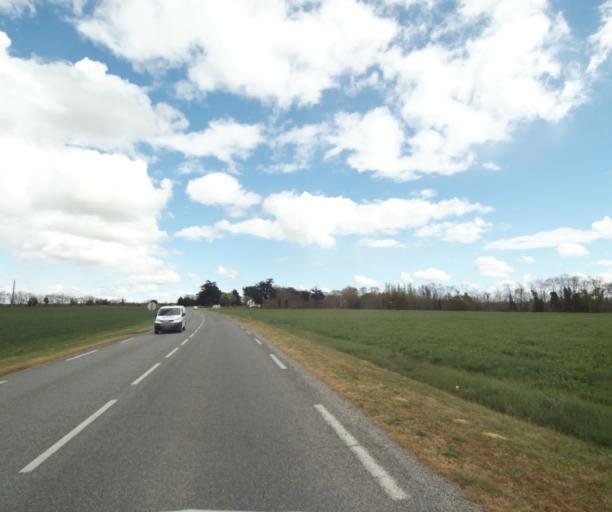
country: FR
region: Midi-Pyrenees
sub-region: Departement de l'Ariege
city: Saverdun
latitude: 43.2309
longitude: 1.5952
